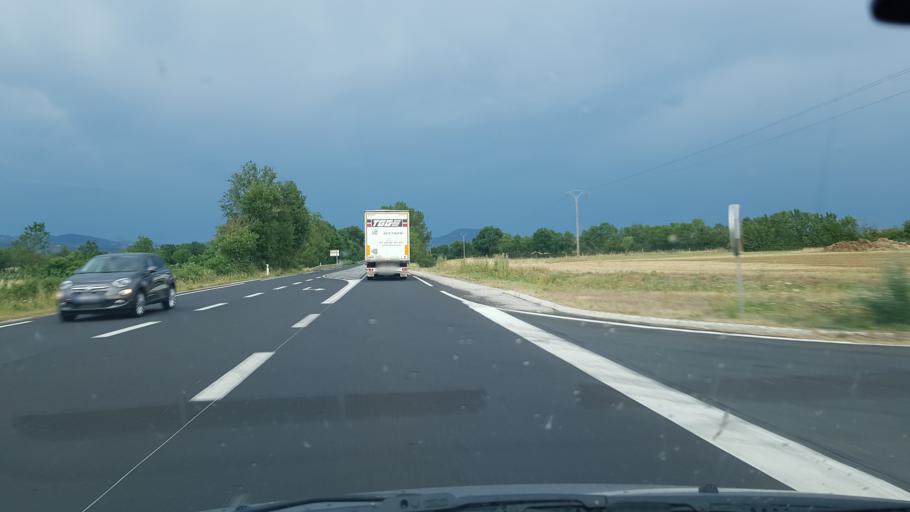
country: FR
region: Auvergne
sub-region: Departement de la Haute-Loire
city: Paulhaguet
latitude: 45.1785
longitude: 3.5184
